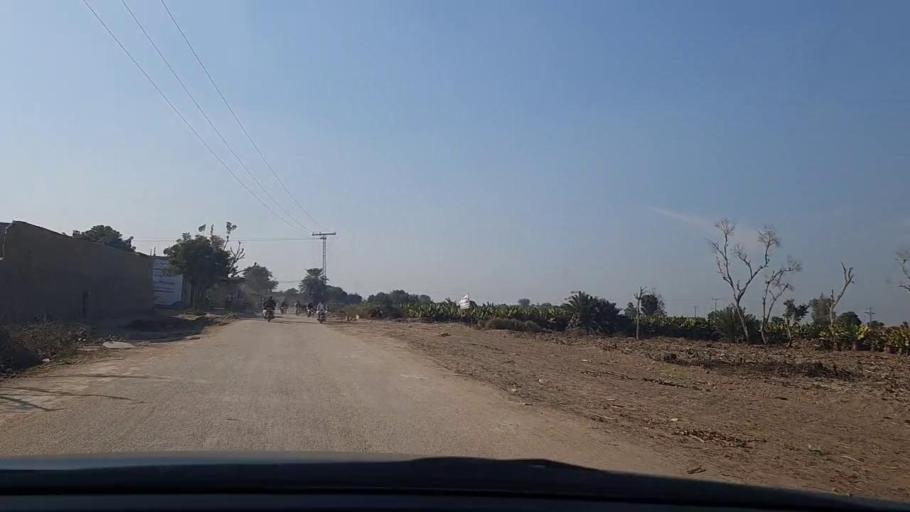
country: PK
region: Sindh
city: Daulatpur
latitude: 26.3045
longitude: 68.0908
